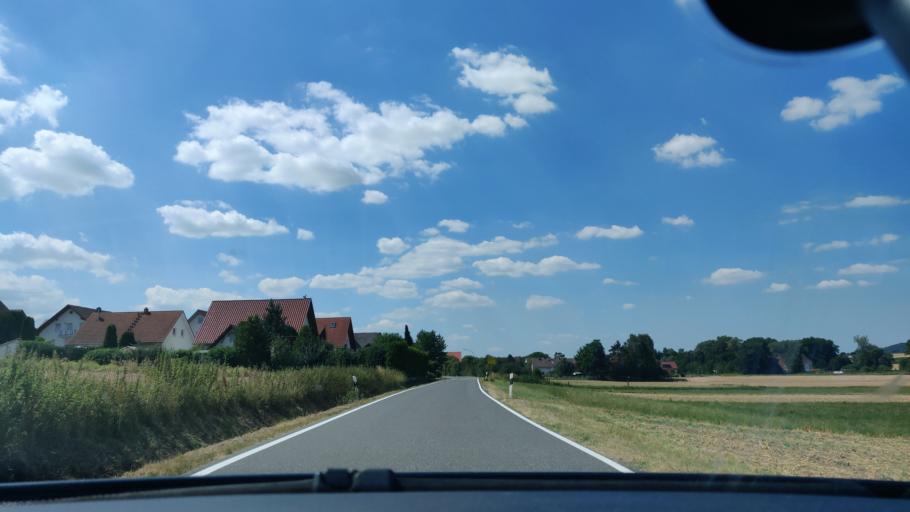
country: DE
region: Hesse
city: Gudensberg
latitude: 51.1501
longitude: 9.3880
